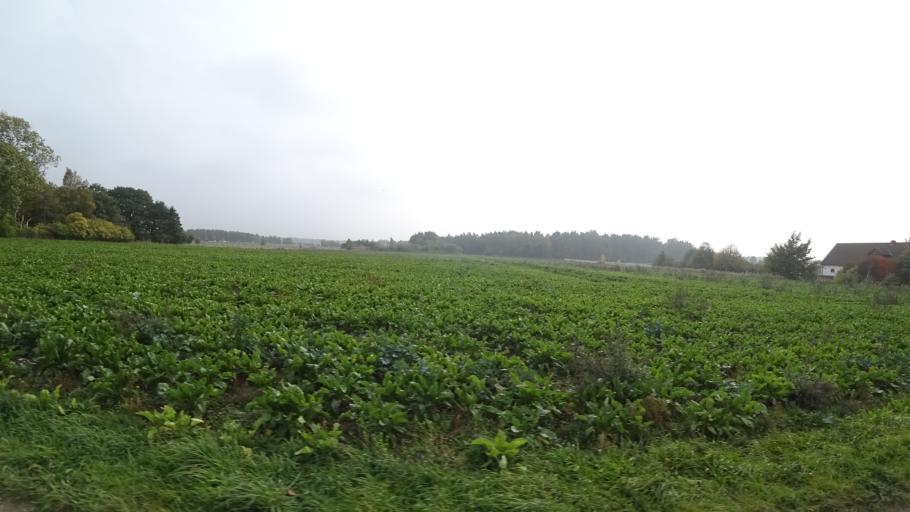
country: SE
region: Skane
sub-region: Kavlinge Kommun
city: Hofterup
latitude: 55.8064
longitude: 12.9914
